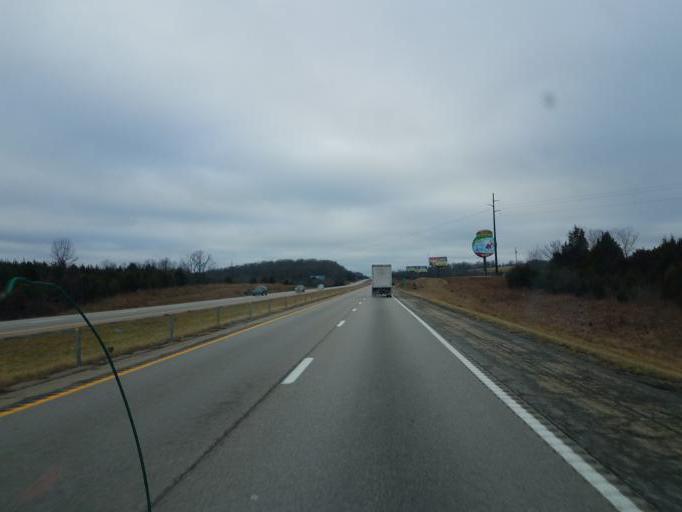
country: US
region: Missouri
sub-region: Laclede County
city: Lebanon
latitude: 37.5734
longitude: -92.7635
